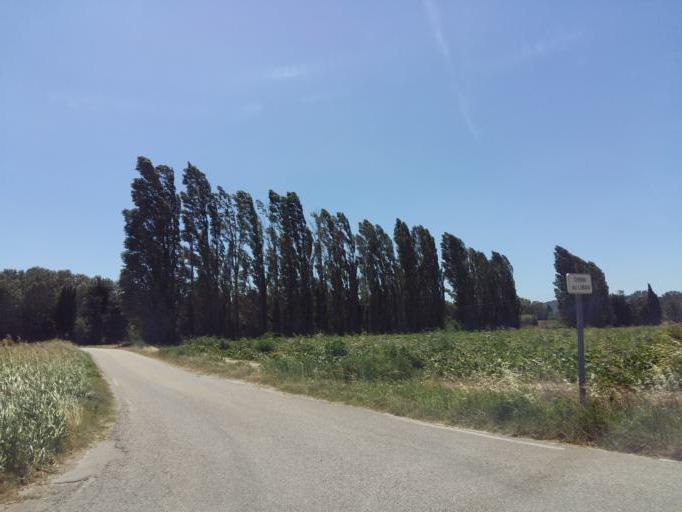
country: FR
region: Provence-Alpes-Cote d'Azur
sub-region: Departement du Vaucluse
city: Mornas
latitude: 44.1876
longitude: 4.7294
